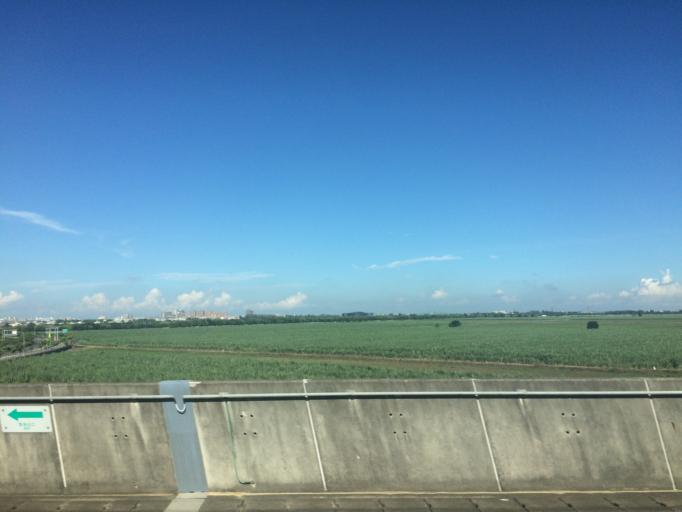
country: TW
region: Taiwan
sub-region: Chiayi
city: Taibao
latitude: 23.4723
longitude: 120.3245
